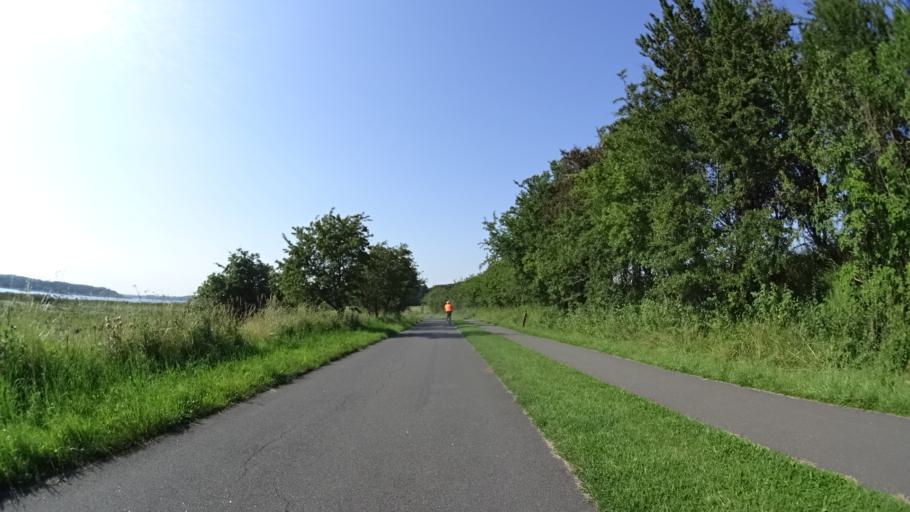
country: DK
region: Central Jutland
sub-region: Arhus Kommune
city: Stavtrup
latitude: 56.1438
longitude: 10.1377
